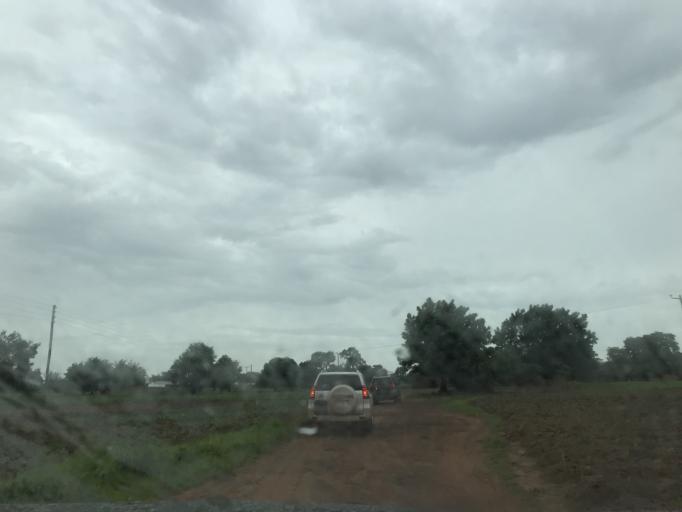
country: GH
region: Upper West
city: Wa
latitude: 10.5134
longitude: -2.7051
